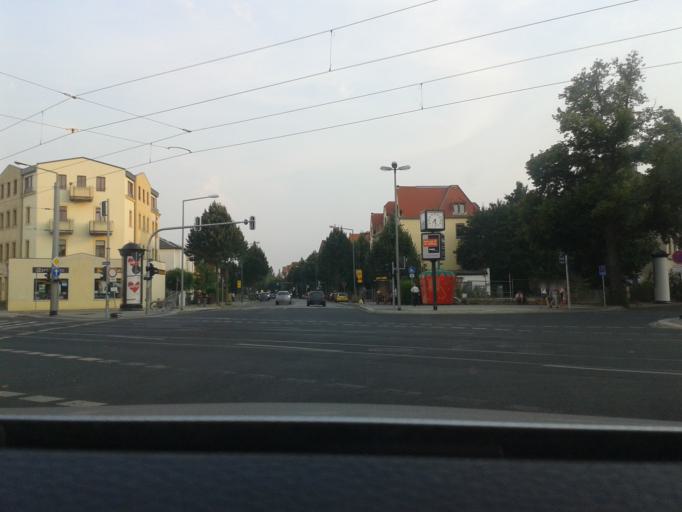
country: DE
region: Saxony
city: Albertstadt
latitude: 51.0396
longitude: 13.8059
